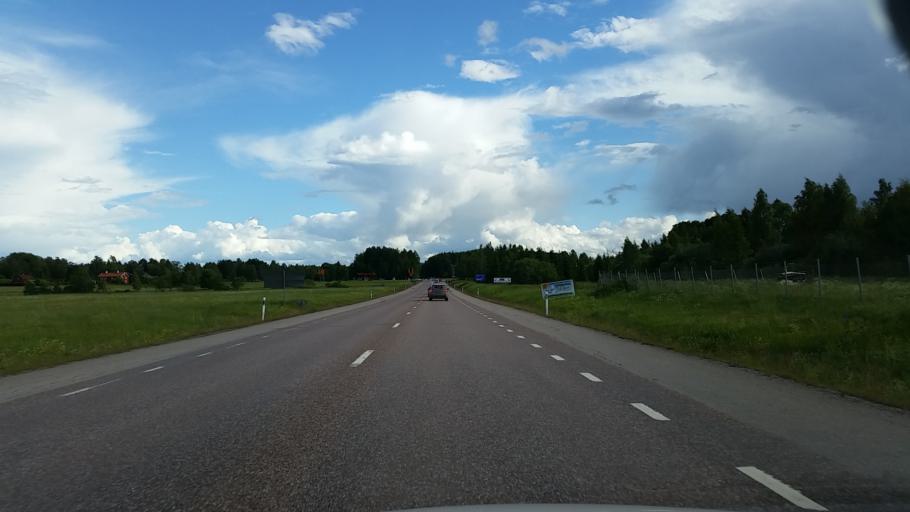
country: SE
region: Dalarna
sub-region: Smedjebackens Kommun
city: Smedjebacken
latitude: 60.0759
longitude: 15.5442
